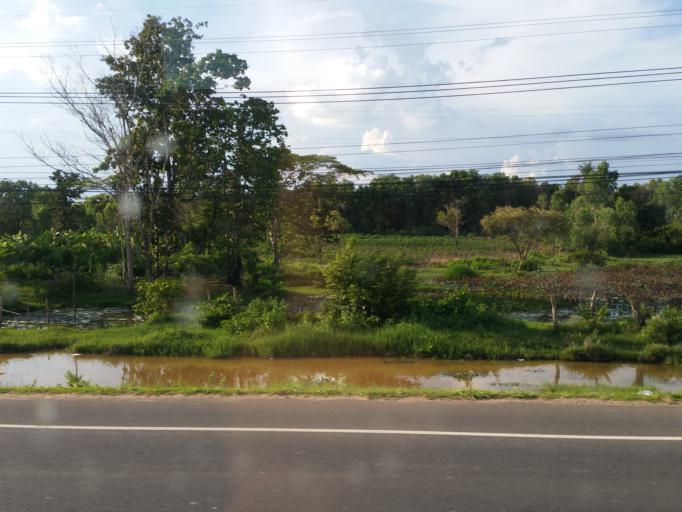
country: TH
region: Changwat Ubon Ratchathani
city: Sirindhorn
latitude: 15.2011
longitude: 105.3780
